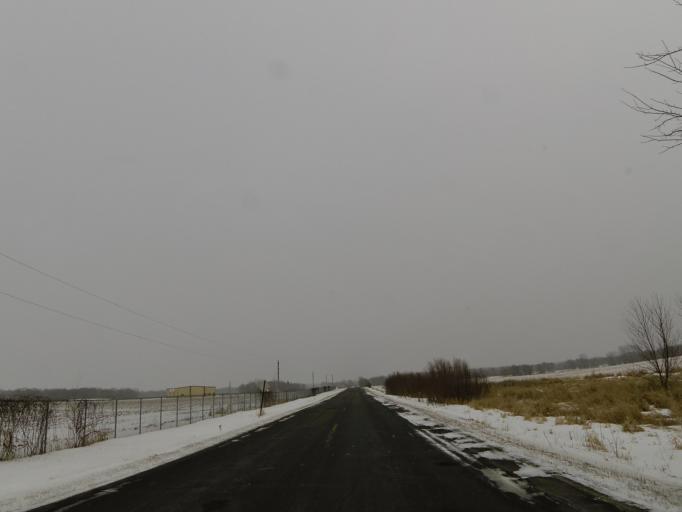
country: US
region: Minnesota
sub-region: Washington County
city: Lake Elmo
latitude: 44.9925
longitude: -92.8593
